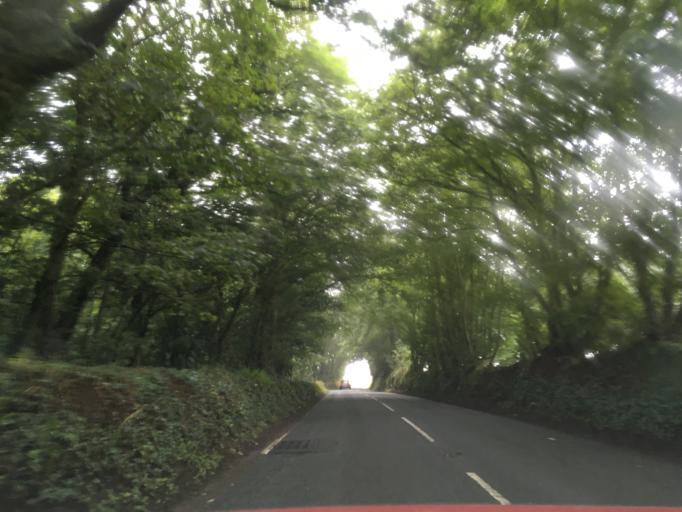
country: GB
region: Wales
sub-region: Pembrokeshire
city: Saint David's
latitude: 51.8755
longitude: -5.2045
